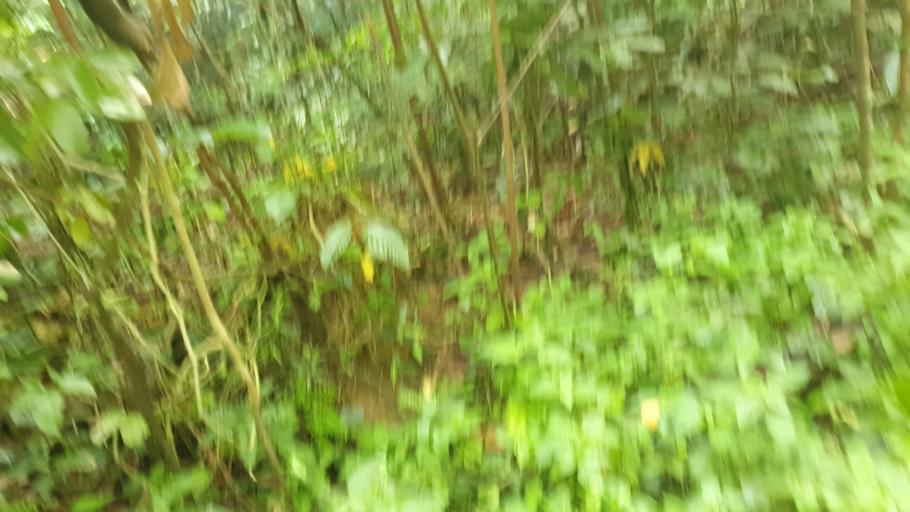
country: SG
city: Singapore
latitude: 1.3602
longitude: 103.8233
